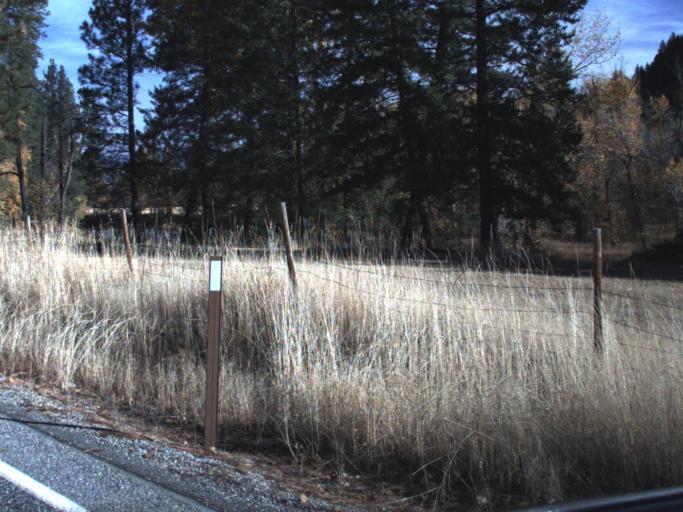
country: CA
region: British Columbia
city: Grand Forks
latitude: 48.9394
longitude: -118.5580
